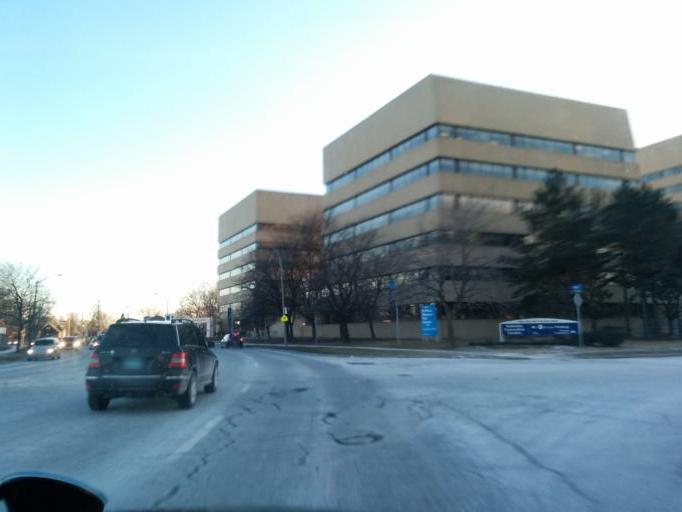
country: CA
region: Ontario
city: Etobicoke
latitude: 43.6384
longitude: -79.5572
